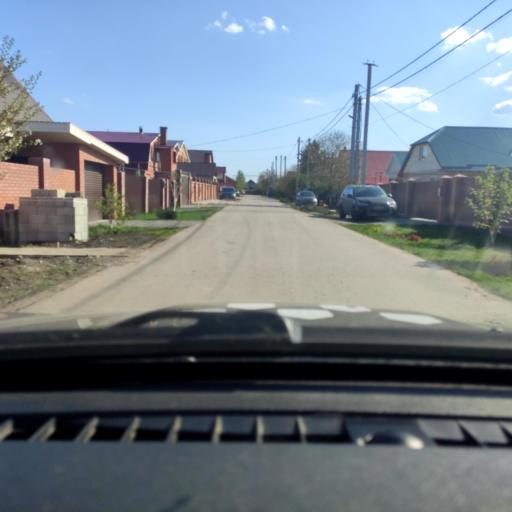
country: RU
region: Samara
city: Tol'yatti
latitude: 53.5635
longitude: 49.3784
